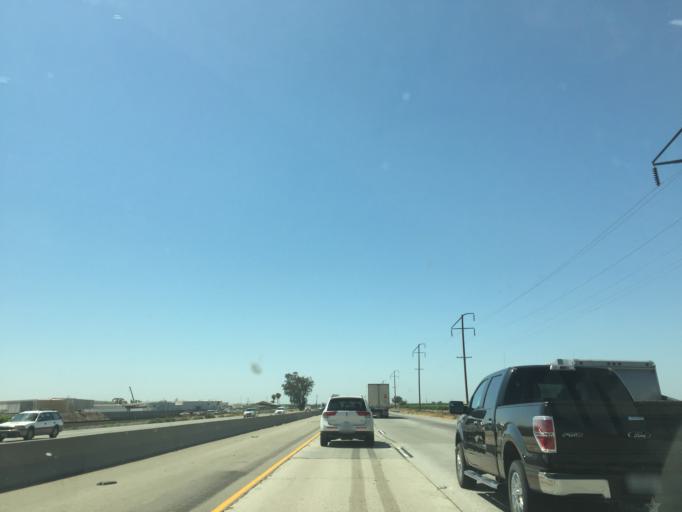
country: US
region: California
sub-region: Kern County
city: Rosedale
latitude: 35.4816
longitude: -119.1403
